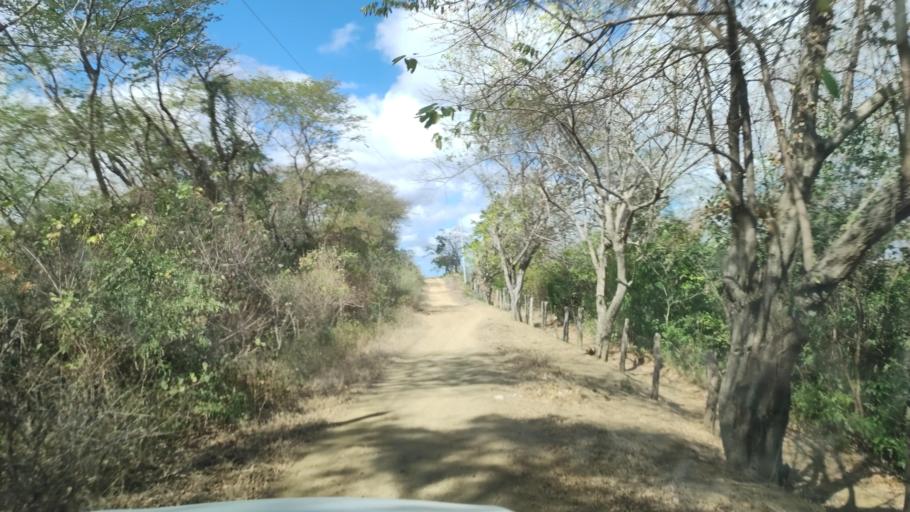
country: NI
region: Carazo
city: Santa Teresa
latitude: 11.6520
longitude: -86.2052
